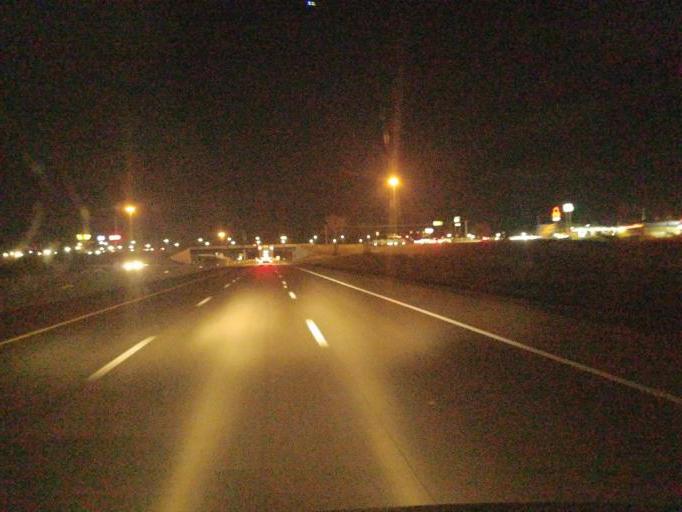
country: US
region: Ohio
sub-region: Montgomery County
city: Huber Heights
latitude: 39.8699
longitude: -84.1409
